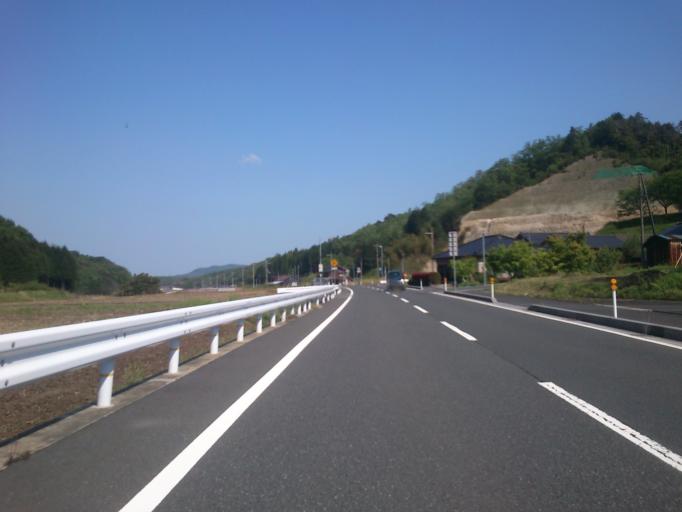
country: JP
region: Kyoto
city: Miyazu
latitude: 35.6496
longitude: 135.1232
